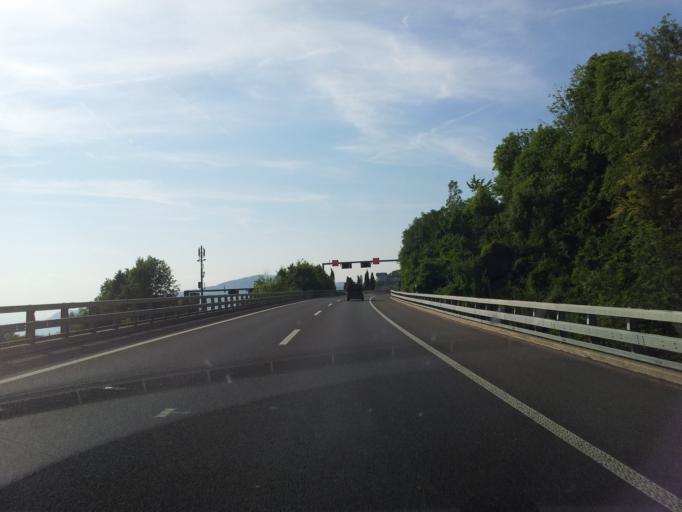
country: CH
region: Vaud
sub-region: Riviera-Pays-d'Enhaut District
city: Montreux
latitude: 46.4348
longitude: 6.9193
